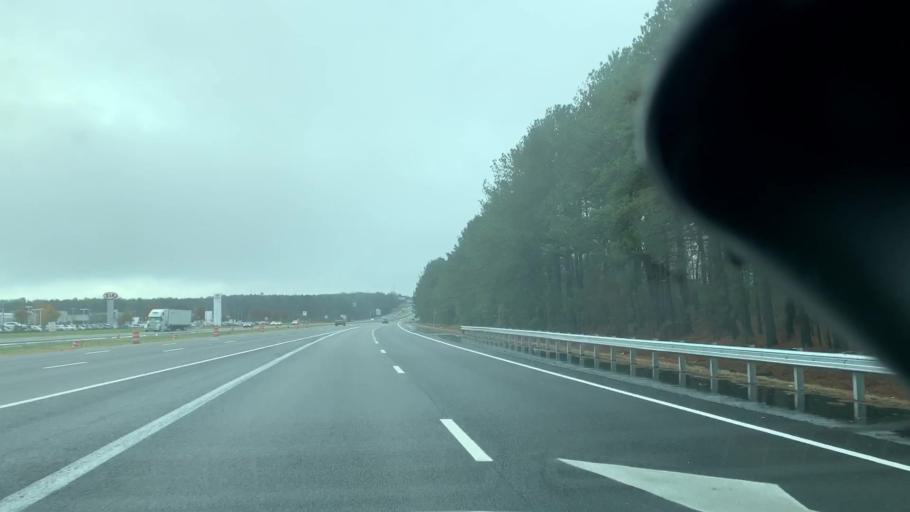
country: US
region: South Carolina
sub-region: Richland County
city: Dentsville
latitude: 34.1311
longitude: -80.9631
